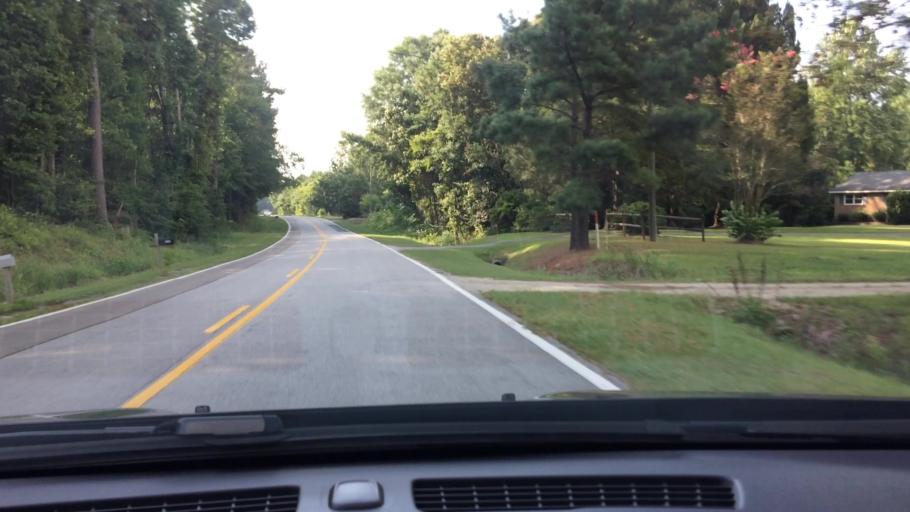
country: US
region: North Carolina
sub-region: Beaufort County
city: River Road
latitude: 35.4495
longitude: -77.0161
